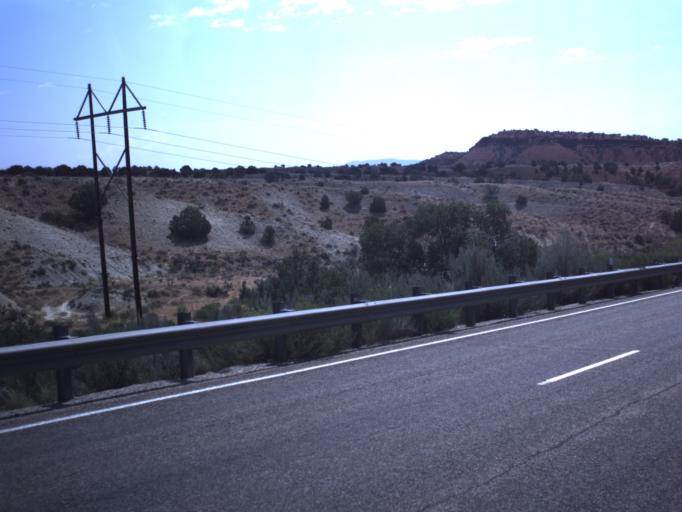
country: US
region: Utah
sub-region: Uintah County
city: Vernal
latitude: 40.6046
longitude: -109.4676
